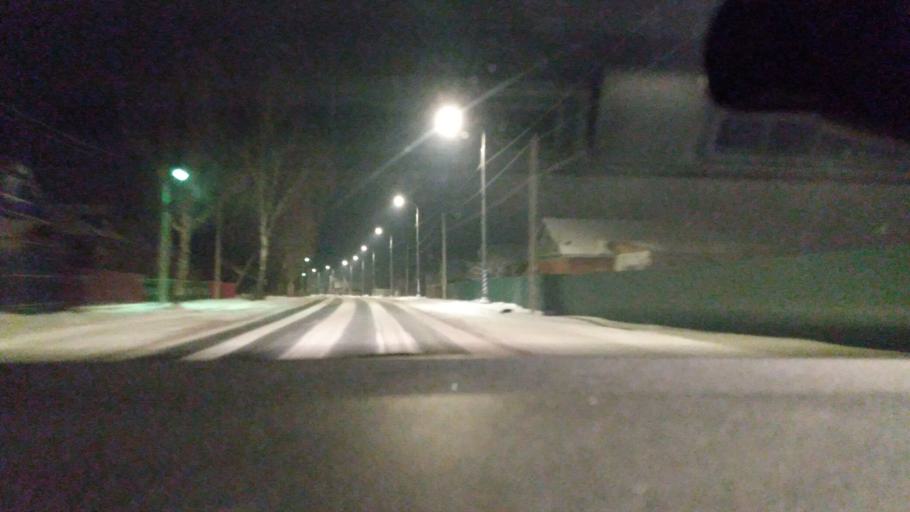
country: RU
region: Moskovskaya
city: Krasnaya Poyma
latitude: 55.1014
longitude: 38.9907
